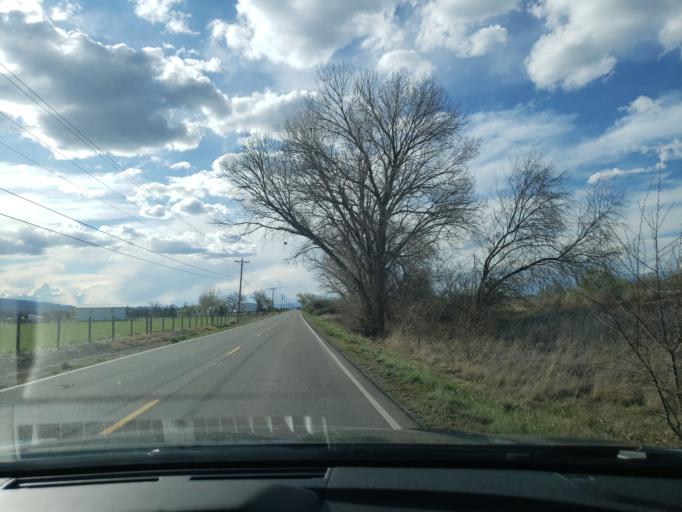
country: US
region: Colorado
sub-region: Mesa County
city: Redlands
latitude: 39.1233
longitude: -108.6720
